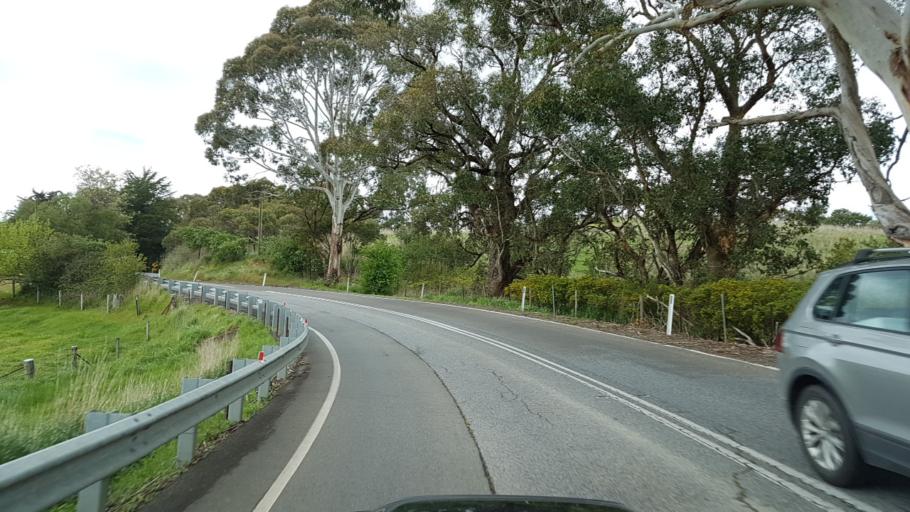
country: AU
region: South Australia
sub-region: Adelaide Hills
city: Lobethal
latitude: -34.9120
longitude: 138.8490
